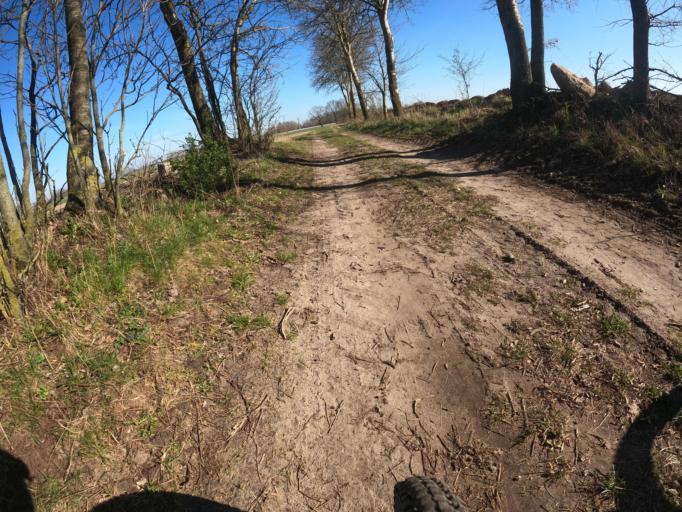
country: PL
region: West Pomeranian Voivodeship
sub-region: Powiat kolobrzeski
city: Ryman
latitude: 54.0195
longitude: 15.4745
